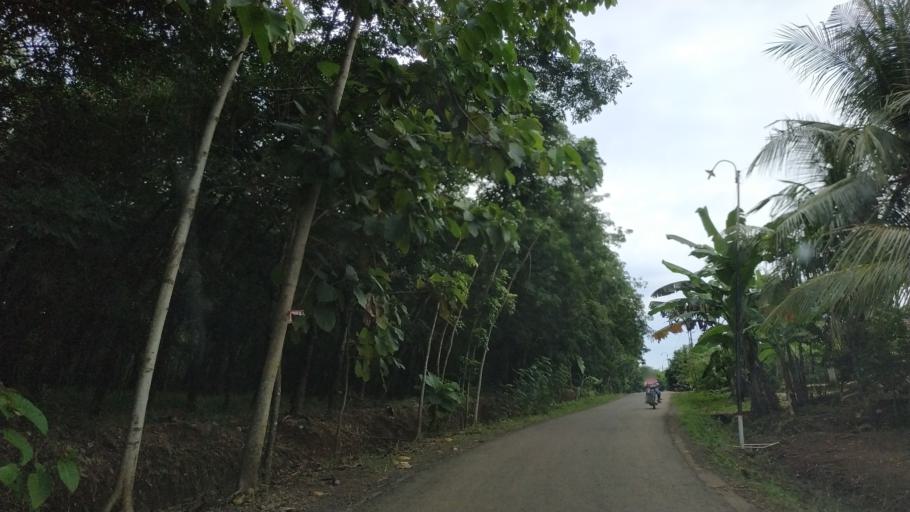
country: ID
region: Central Java
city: Krajan Tegalombo
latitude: -6.4360
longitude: 110.9820
